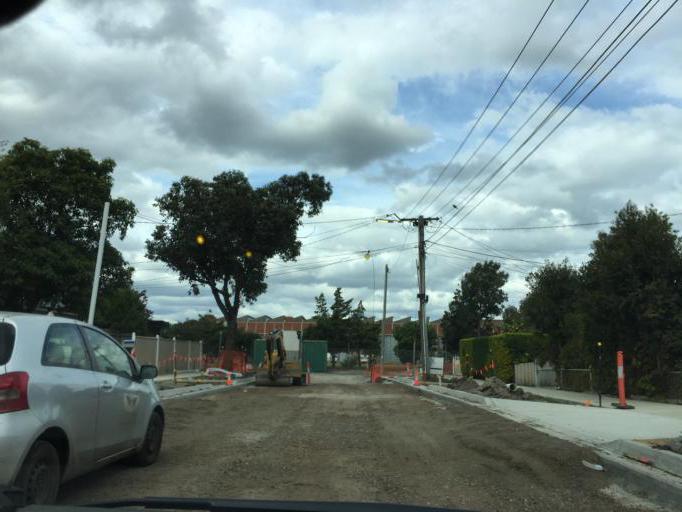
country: AU
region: Victoria
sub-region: Maribyrnong
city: West Footscray
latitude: -37.8009
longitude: 144.8665
